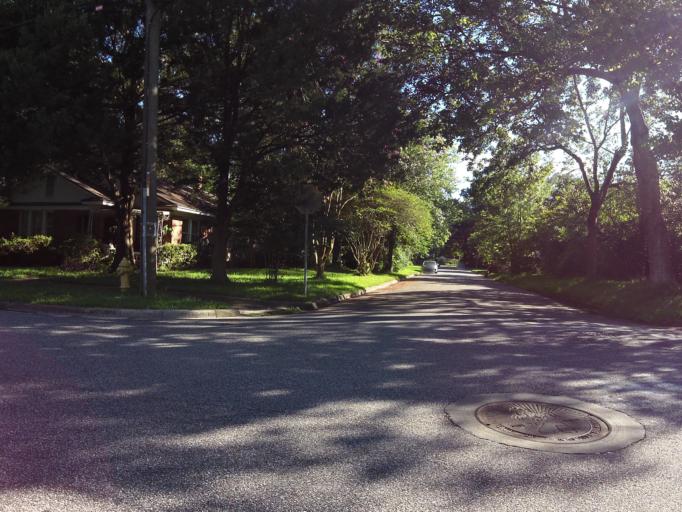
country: US
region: Florida
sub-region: Duval County
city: Jacksonville
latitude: 30.3032
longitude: -81.7142
